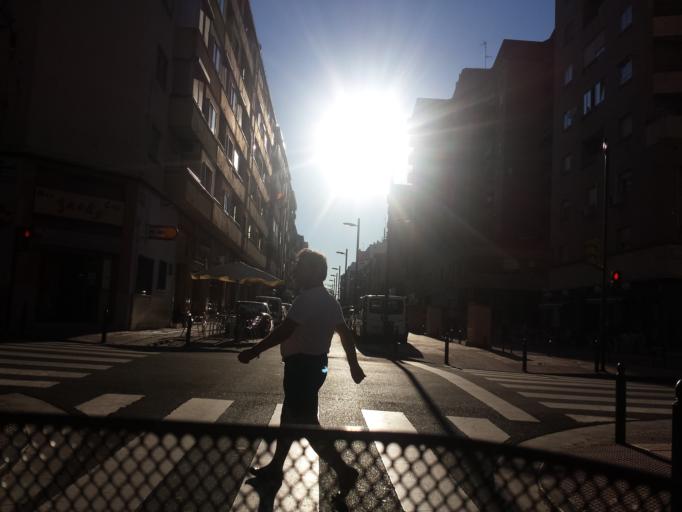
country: ES
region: Aragon
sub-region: Provincia de Zaragoza
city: Almozara
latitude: 41.6558
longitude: -0.9025
